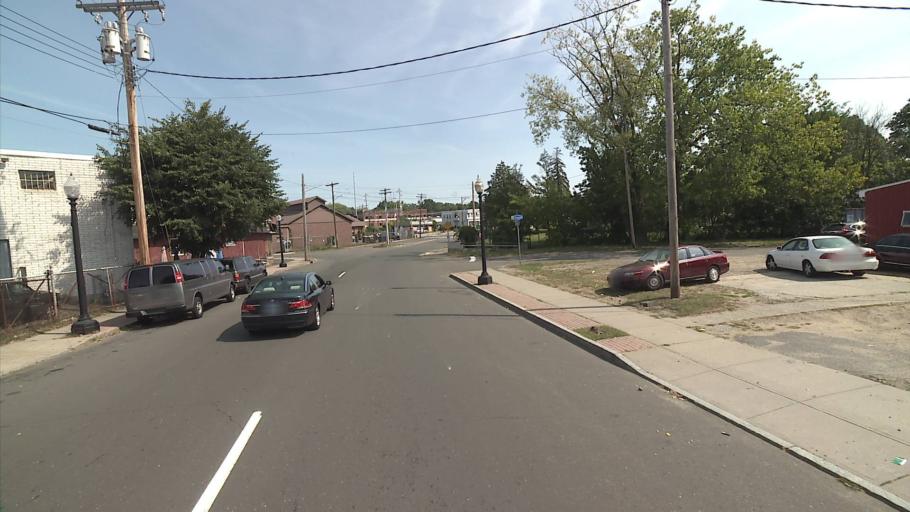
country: US
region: Connecticut
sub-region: Fairfield County
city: Stratford
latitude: 41.1833
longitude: -73.1549
